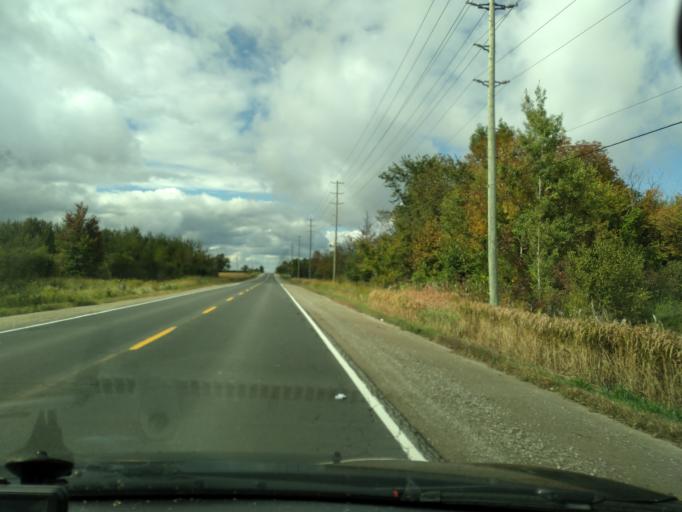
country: CA
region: Ontario
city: Innisfil
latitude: 44.2823
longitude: -79.6921
